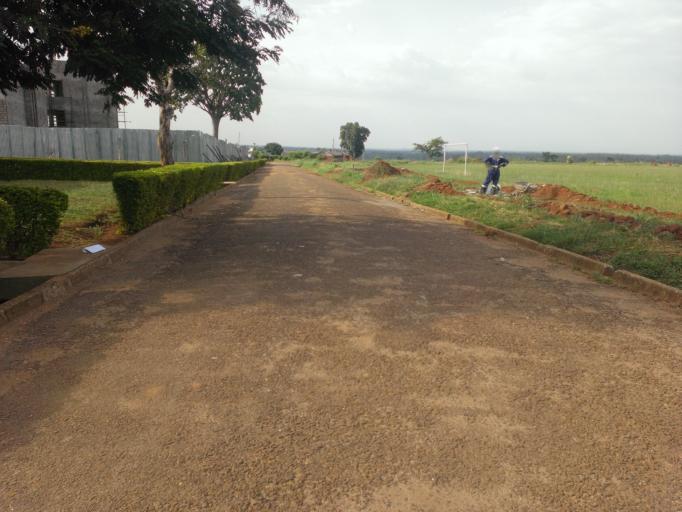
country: UG
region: Eastern Region
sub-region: Busia District
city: Busia
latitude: 0.5473
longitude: 34.0216
